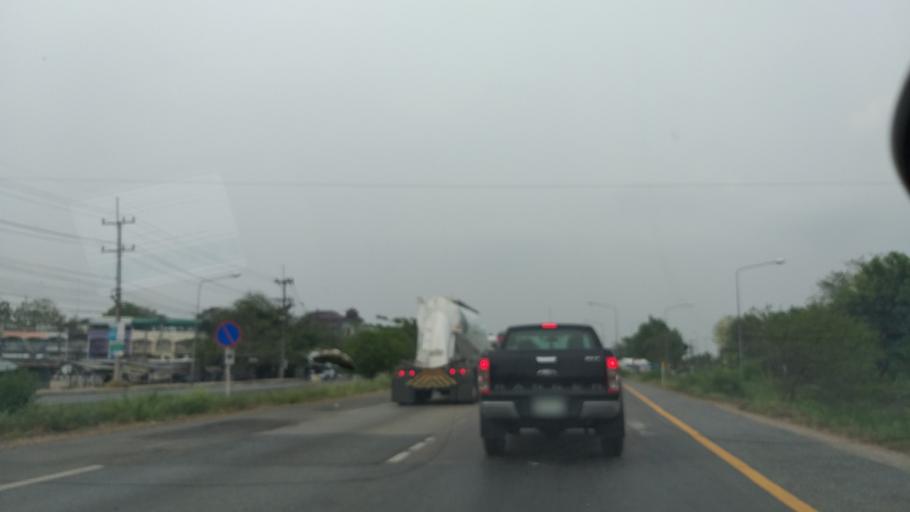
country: TH
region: Chon Buri
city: Ban Bueng
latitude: 13.2822
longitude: 101.2556
